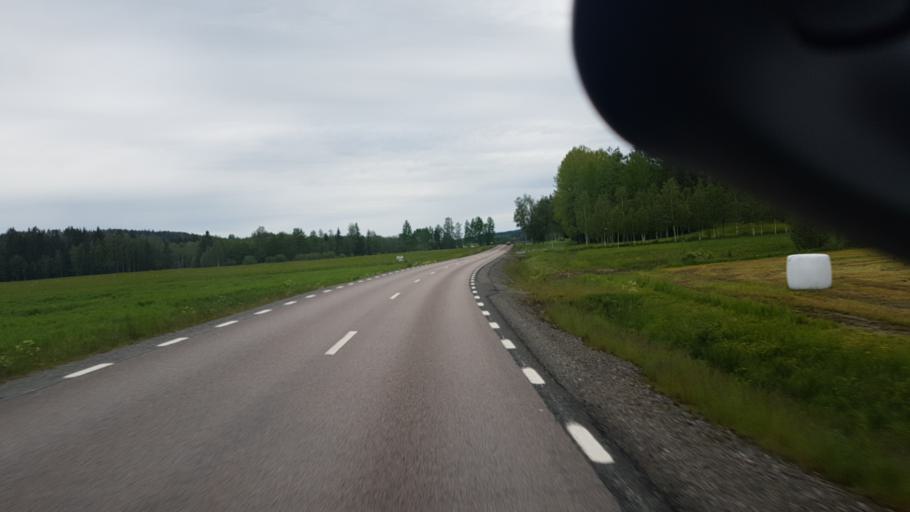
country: SE
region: Vaermland
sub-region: Arjangs Kommun
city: Arjaeng
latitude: 59.6362
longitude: 12.1355
